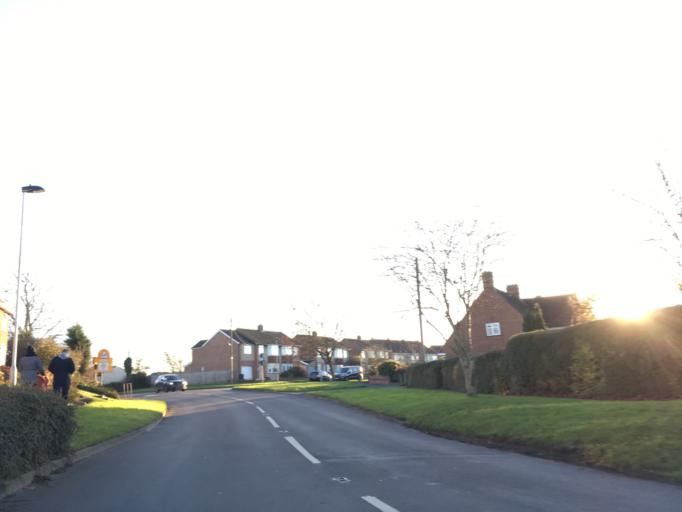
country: GB
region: England
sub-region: South Gloucestershire
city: Thornbury
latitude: 51.6136
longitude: -2.5137
